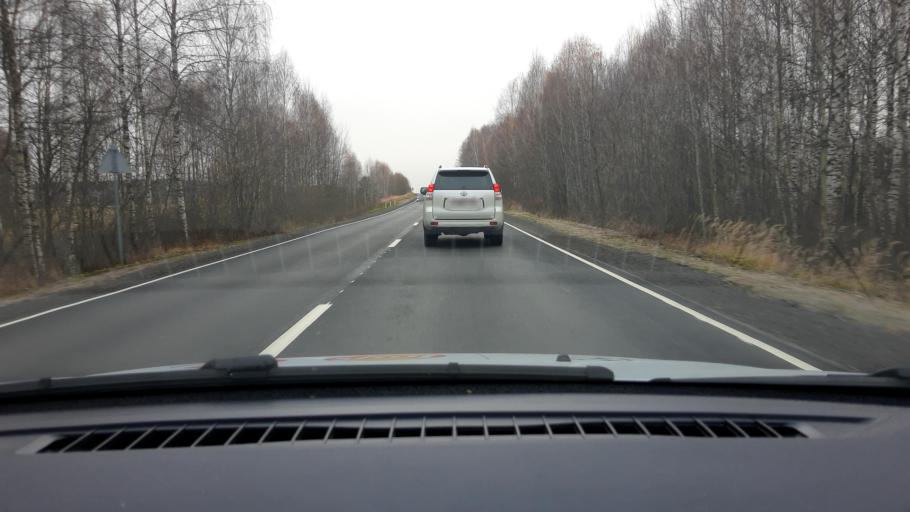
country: RU
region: Nizjnij Novgorod
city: Novaya Balakhna
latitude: 56.5892
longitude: 43.6656
